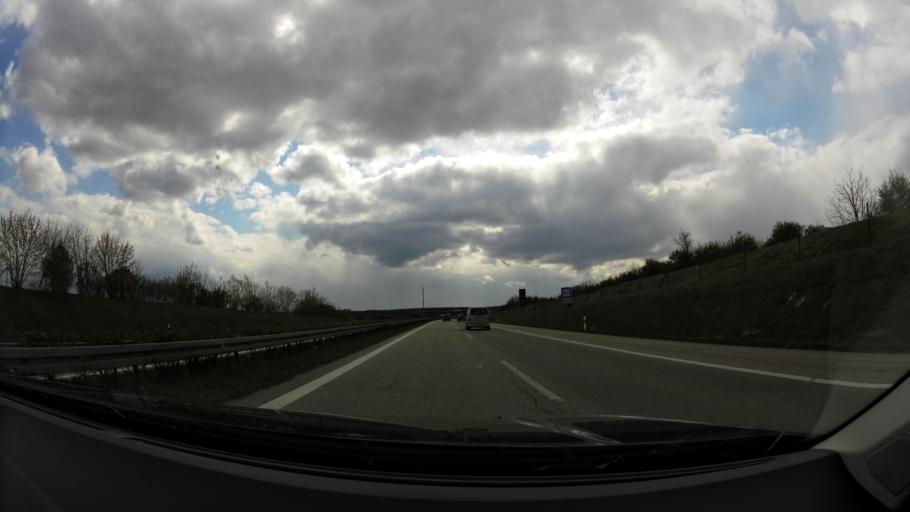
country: DE
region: Mecklenburg-Vorpommern
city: Krakow am See
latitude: 53.6202
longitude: 12.3761
